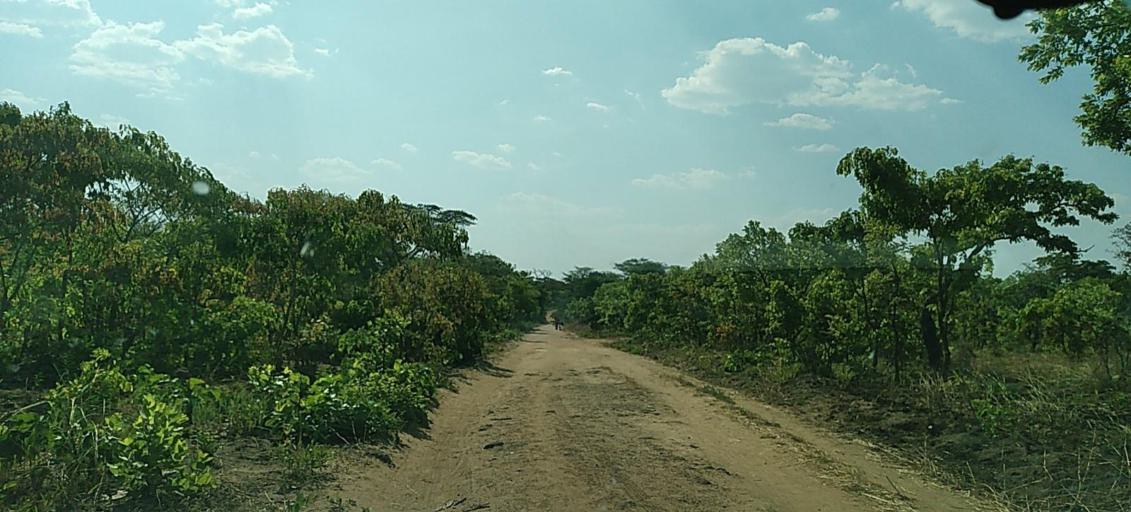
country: ZM
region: North-Western
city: Kalengwa
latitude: -13.1070
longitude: 24.9912
